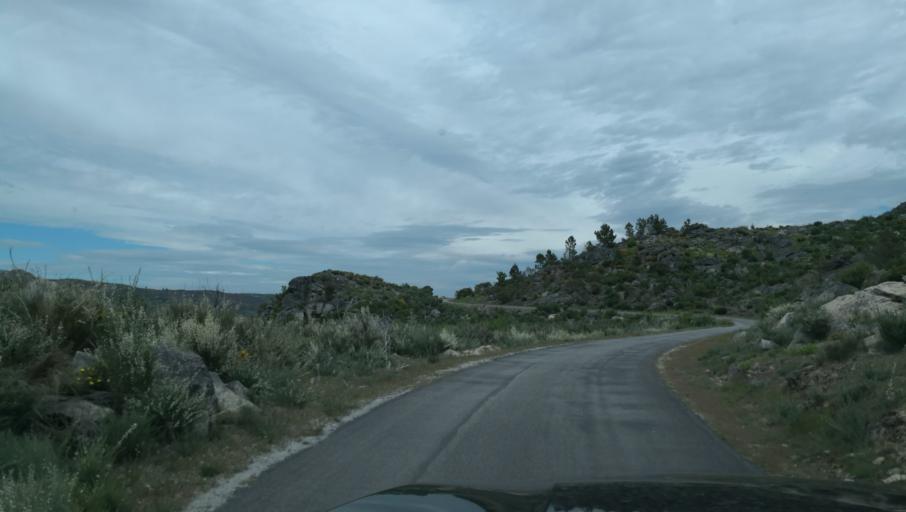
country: PT
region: Vila Real
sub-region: Vila Real
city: Vila Real
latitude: 41.3699
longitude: -7.6993
